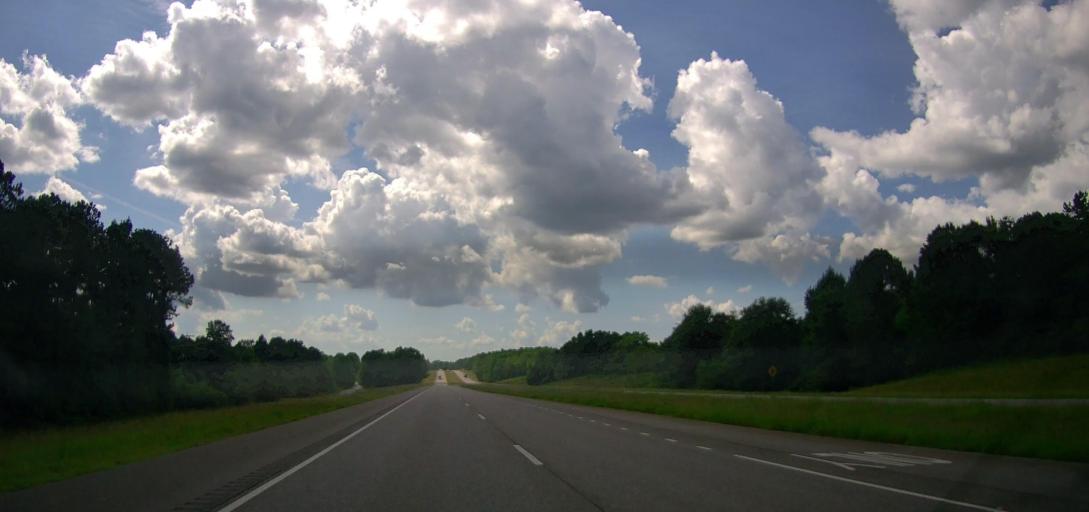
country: US
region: Alabama
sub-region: Pickens County
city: Reform
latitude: 33.3989
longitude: -88.0630
